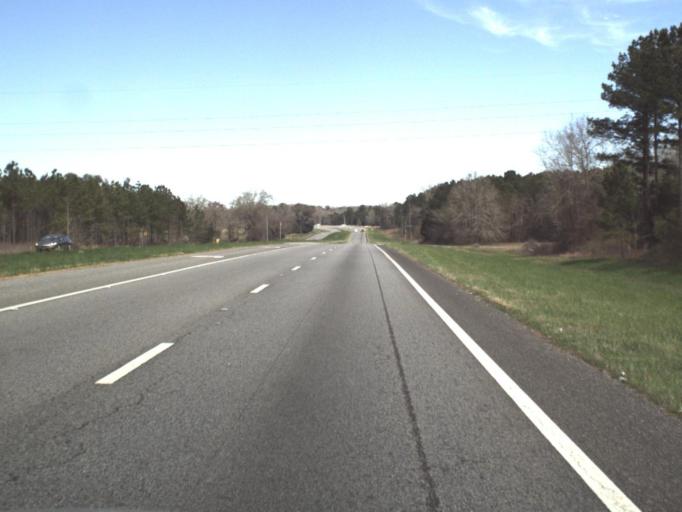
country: US
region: Florida
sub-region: Jackson County
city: Marianna
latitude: 30.8339
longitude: -85.3531
